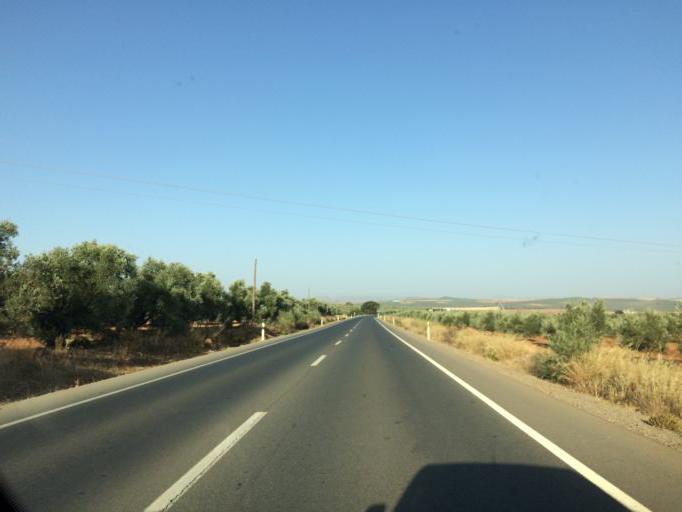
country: ES
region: Andalusia
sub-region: Provincia de Malaga
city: Humilladero
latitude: 37.0568
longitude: -4.7365
